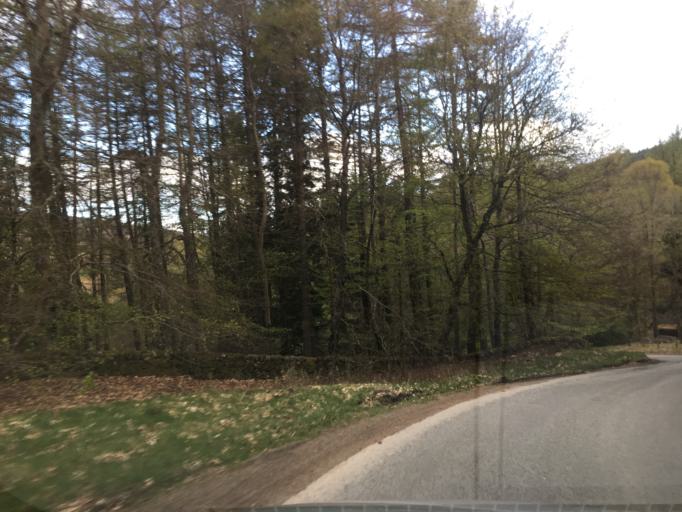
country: GB
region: Scotland
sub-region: Perth and Kinross
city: Aberfeldy
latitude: 56.7581
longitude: -4.0869
